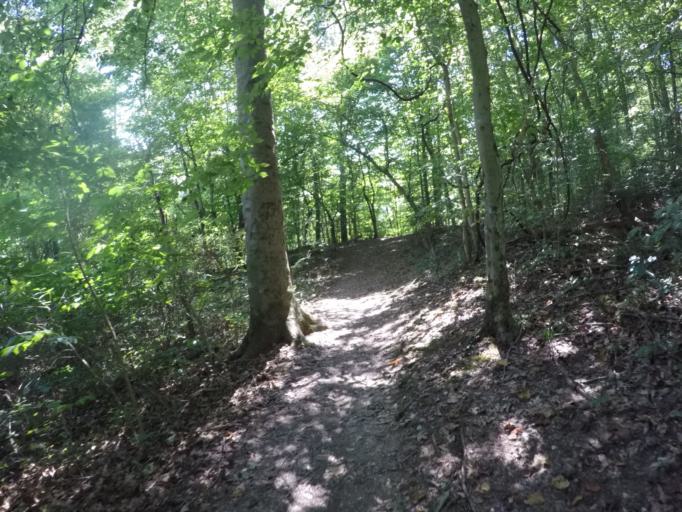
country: US
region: Ohio
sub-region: Lawrence County
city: Ironton
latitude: 38.6143
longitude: -82.6296
